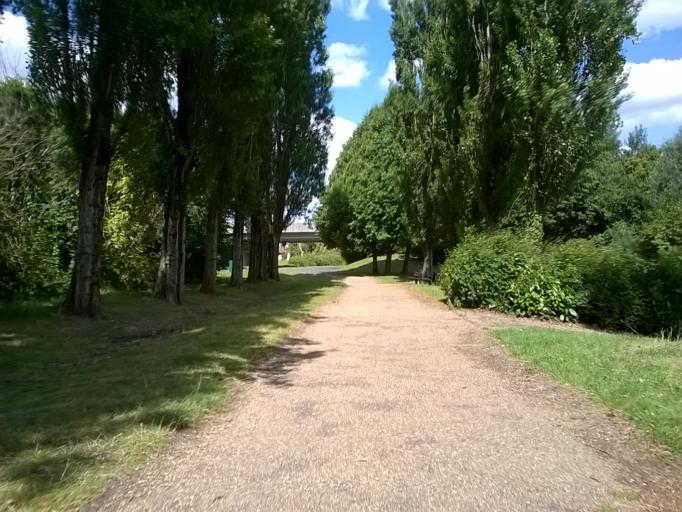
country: GB
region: England
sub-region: Milton Keynes
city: Milton Keynes
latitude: 52.0605
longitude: -0.7378
